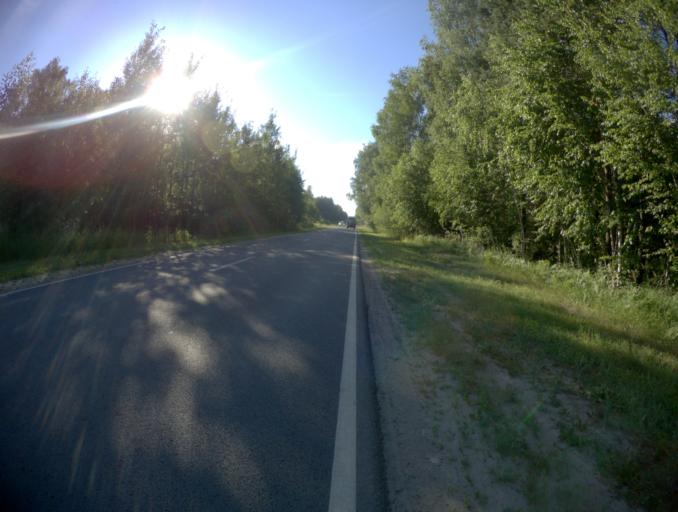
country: RU
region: Nizjnij Novgorod
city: Taremskoye
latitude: 56.0038
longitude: 42.9924
